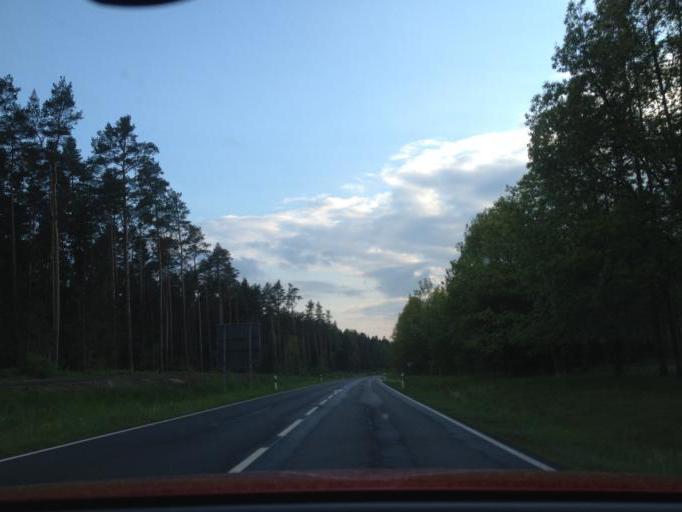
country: DE
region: Bavaria
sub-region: Upper Palatinate
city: Weiherhammer
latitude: 49.6122
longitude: 12.0758
